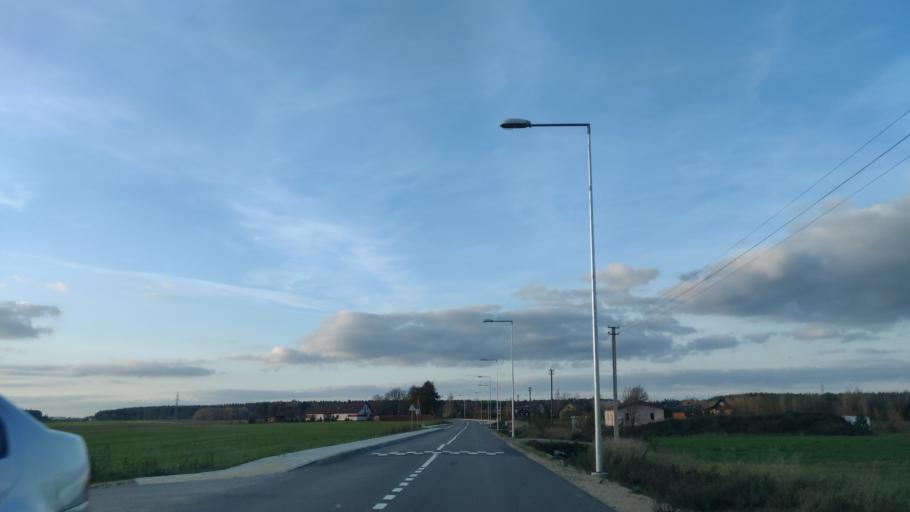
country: LT
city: Lentvaris
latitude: 54.5894
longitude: 25.0499
